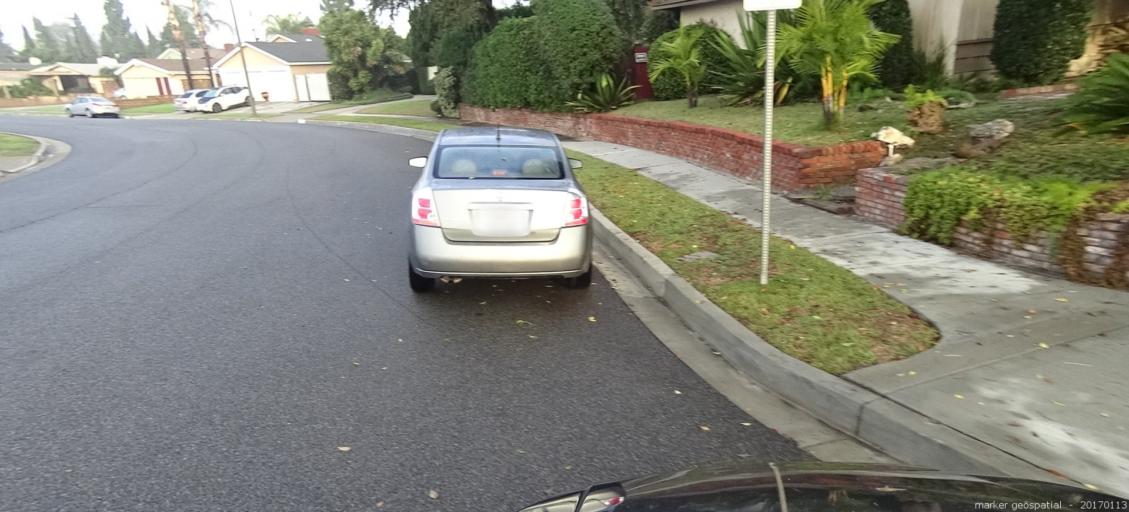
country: US
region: California
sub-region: Orange County
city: Buena Park
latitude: 33.8946
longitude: -117.9904
